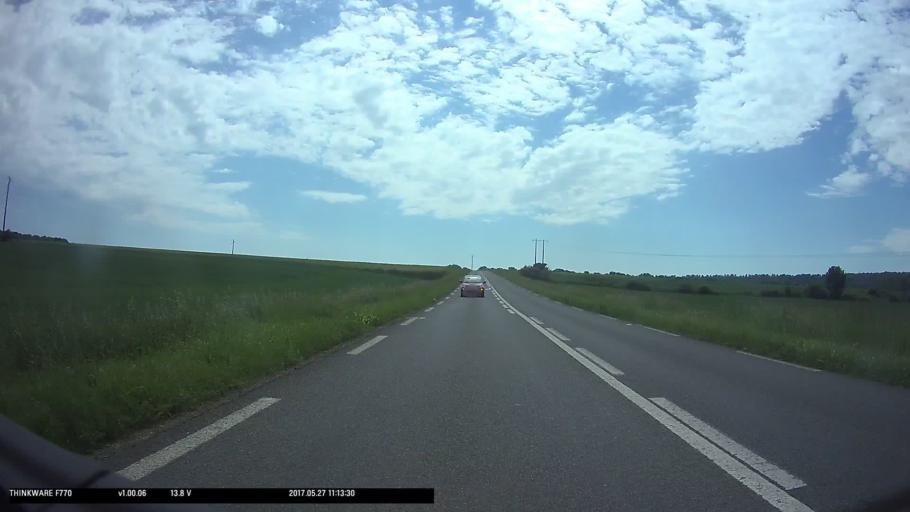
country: FR
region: Picardie
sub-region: Departement de l'Oise
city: Chaumont-en-Vexin
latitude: 49.2783
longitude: 1.8554
